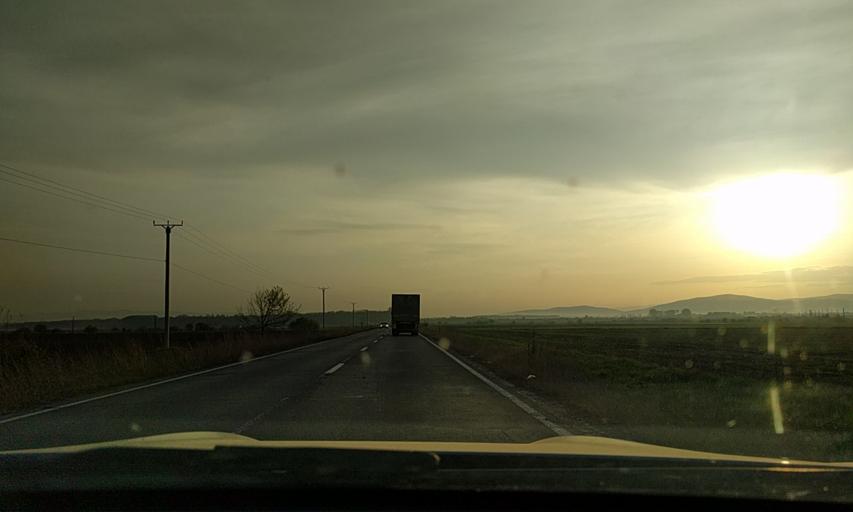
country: RO
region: Brasov
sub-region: Comuna Harman
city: Harman
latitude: 45.7210
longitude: 25.7228
